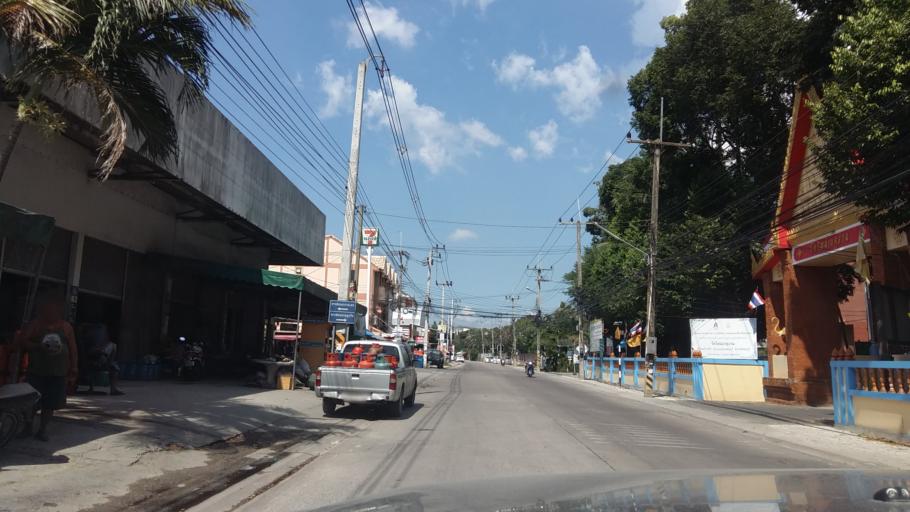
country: TH
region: Chon Buri
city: Chon Buri
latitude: 13.3158
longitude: 100.9306
